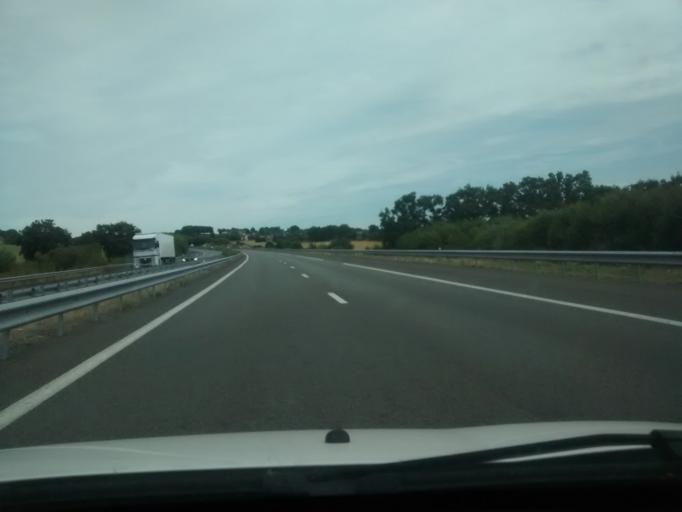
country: FR
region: Brittany
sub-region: Departement d'Ille-et-Vilaine
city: Saint-Jean-sur-Couesnon
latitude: 48.2959
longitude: -1.3666
